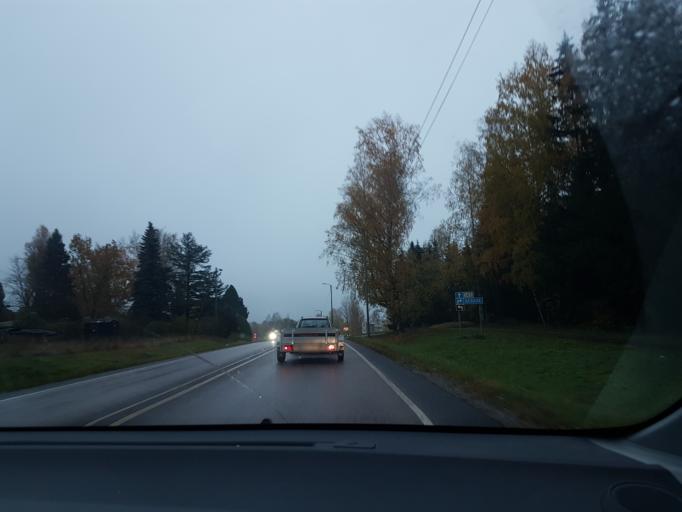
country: FI
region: Uusimaa
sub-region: Helsinki
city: Tuusula
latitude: 60.4125
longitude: 25.0477
